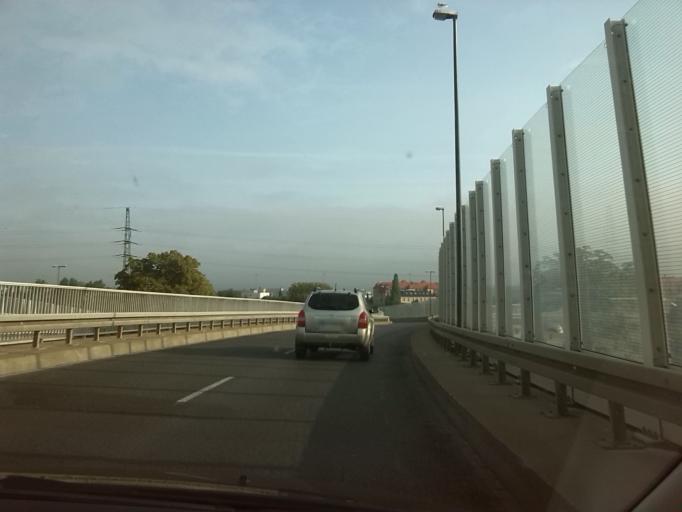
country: DE
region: Saxony
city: Dresden
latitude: 51.0469
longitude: 13.7054
